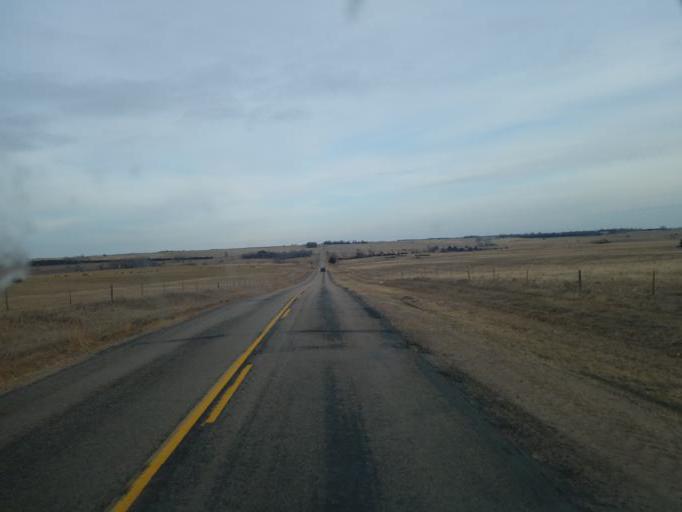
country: US
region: Nebraska
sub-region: Holt County
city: O'Neill
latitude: 42.4659
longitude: -98.2943
